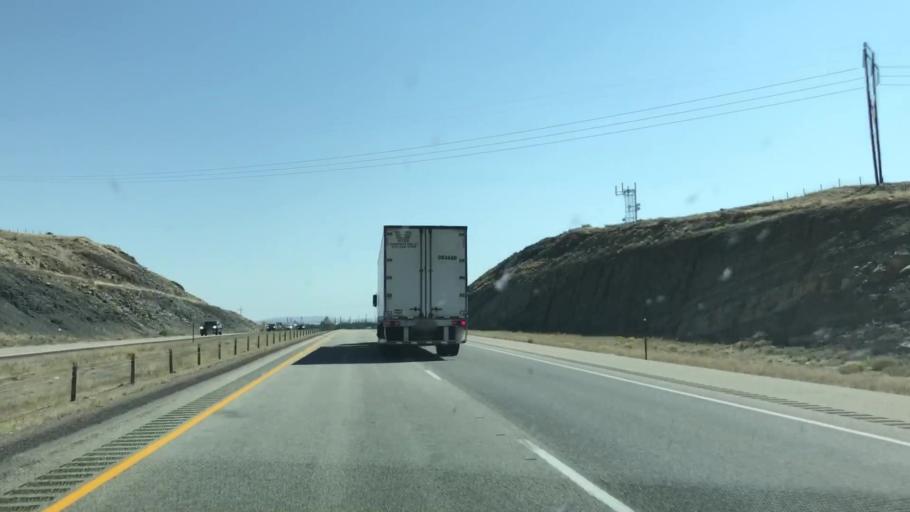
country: US
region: Wyoming
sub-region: Carbon County
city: Rawlins
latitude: 41.7825
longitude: -107.1460
